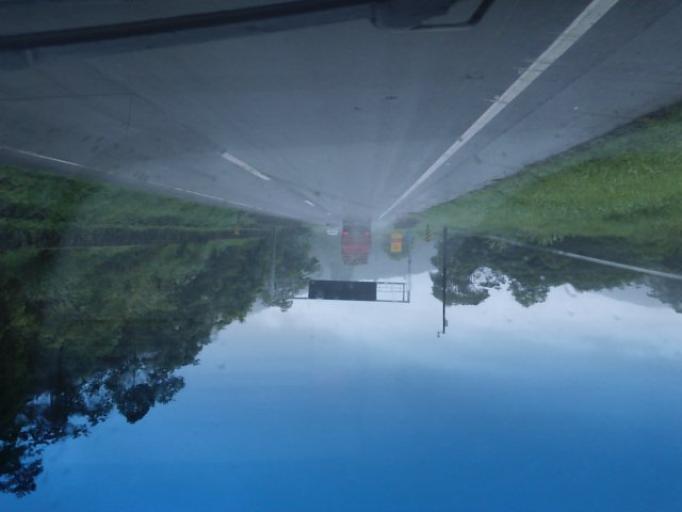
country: BR
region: Sao Paulo
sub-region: Cajati
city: Cajati
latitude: -24.8766
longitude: -48.2094
